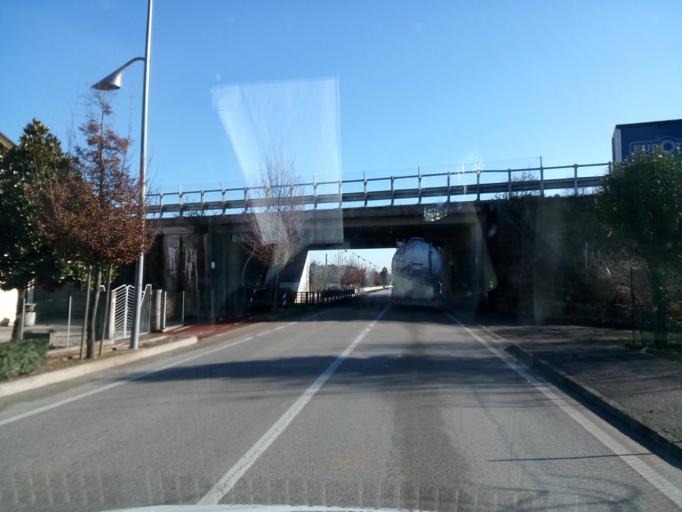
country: IT
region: Veneto
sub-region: Provincia di Treviso
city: Mareno di Piave
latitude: 45.8189
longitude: 12.3126
